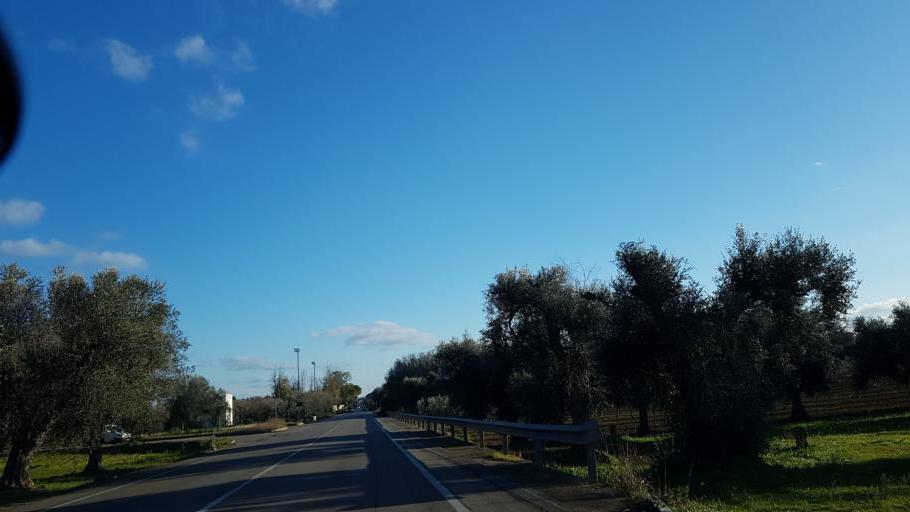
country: IT
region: Apulia
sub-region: Provincia di Lecce
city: Squinzano
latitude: 40.4473
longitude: 18.0310
